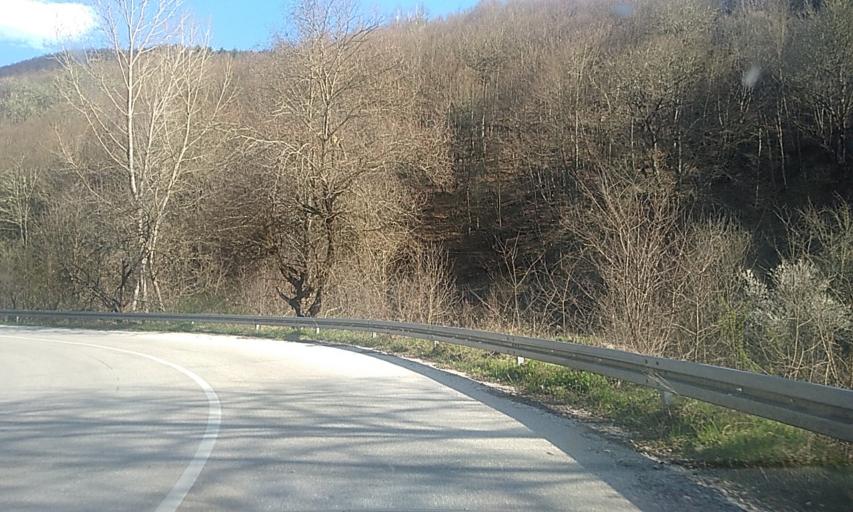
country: RS
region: Central Serbia
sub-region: Pcinjski Okrug
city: Bosilegrad
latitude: 42.4168
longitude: 22.5170
